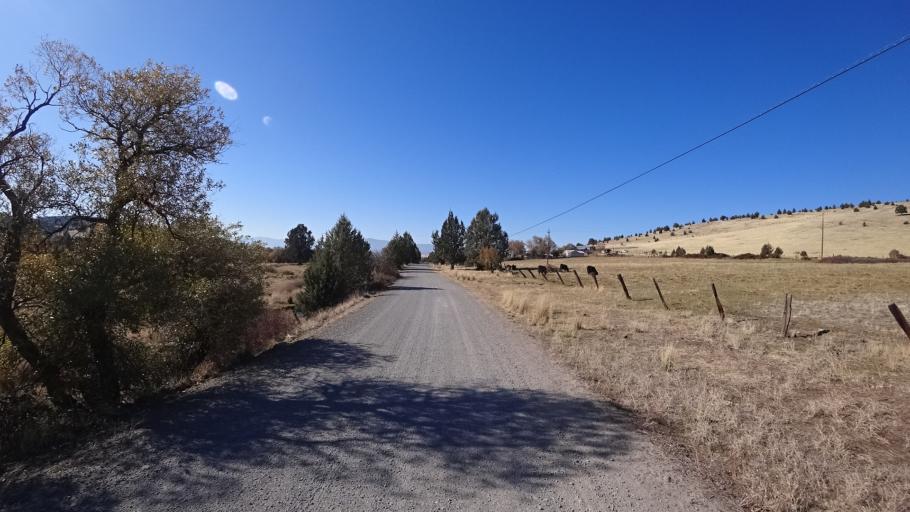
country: US
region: California
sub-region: Siskiyou County
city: Montague
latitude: 41.7295
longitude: -122.3607
